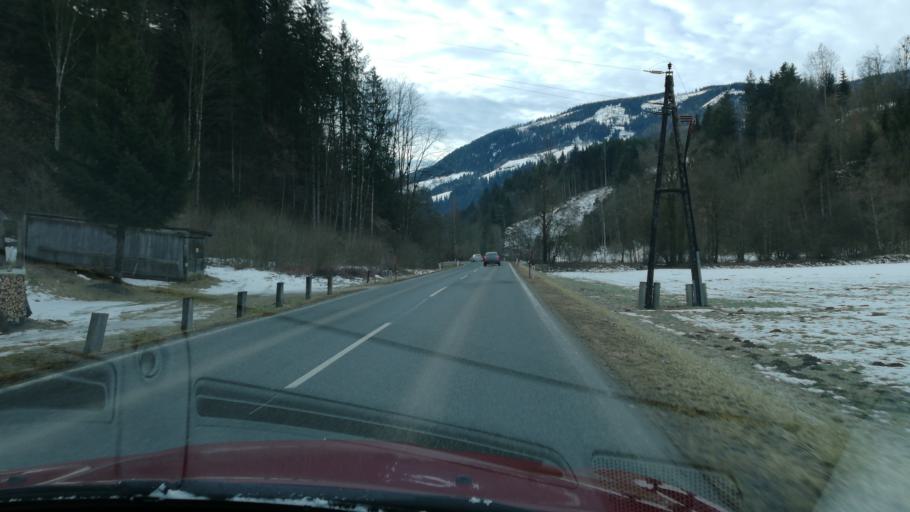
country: AT
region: Styria
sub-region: Politischer Bezirk Liezen
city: Irdning
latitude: 47.4952
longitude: 14.1057
